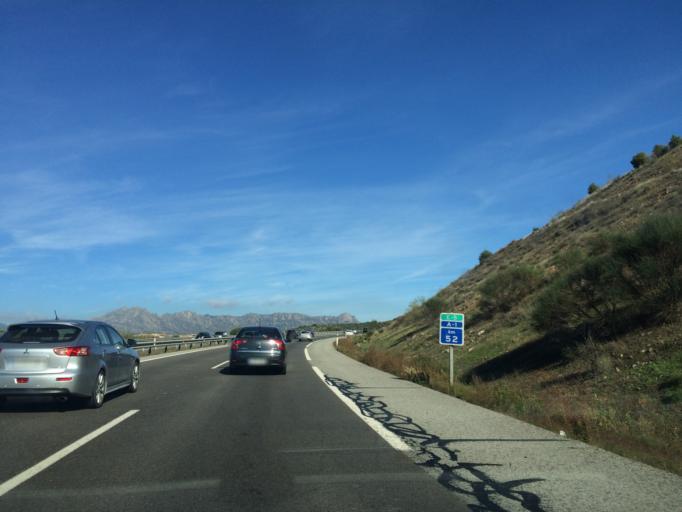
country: ES
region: Madrid
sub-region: Provincia de Madrid
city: Venturada
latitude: 40.8073
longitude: -3.6198
